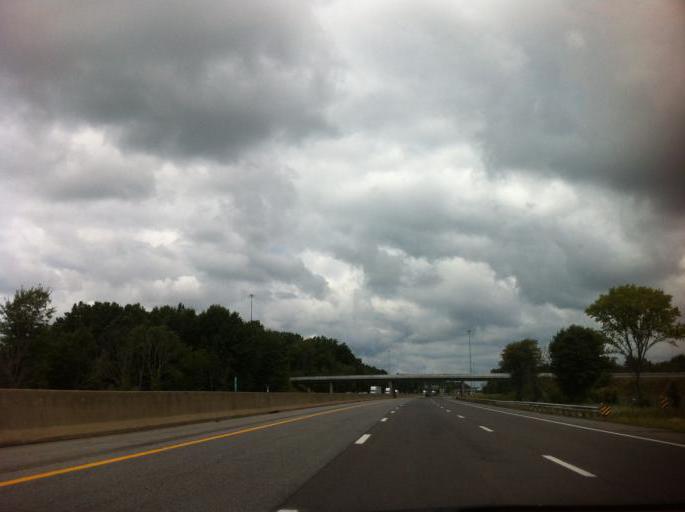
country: US
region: Ohio
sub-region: Trumbull County
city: Lordstown
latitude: 41.1495
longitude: -80.8900
